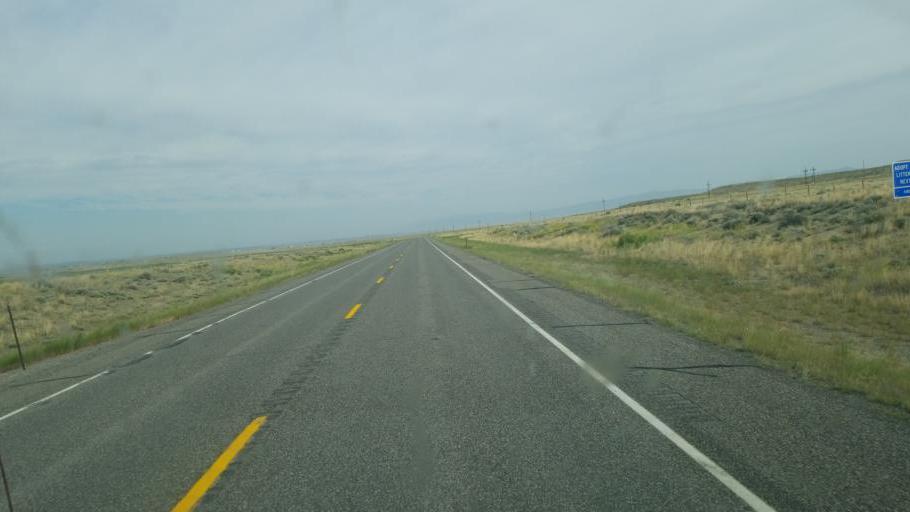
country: US
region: Wyoming
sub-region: Fremont County
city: Riverton
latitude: 43.2271
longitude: -108.0539
